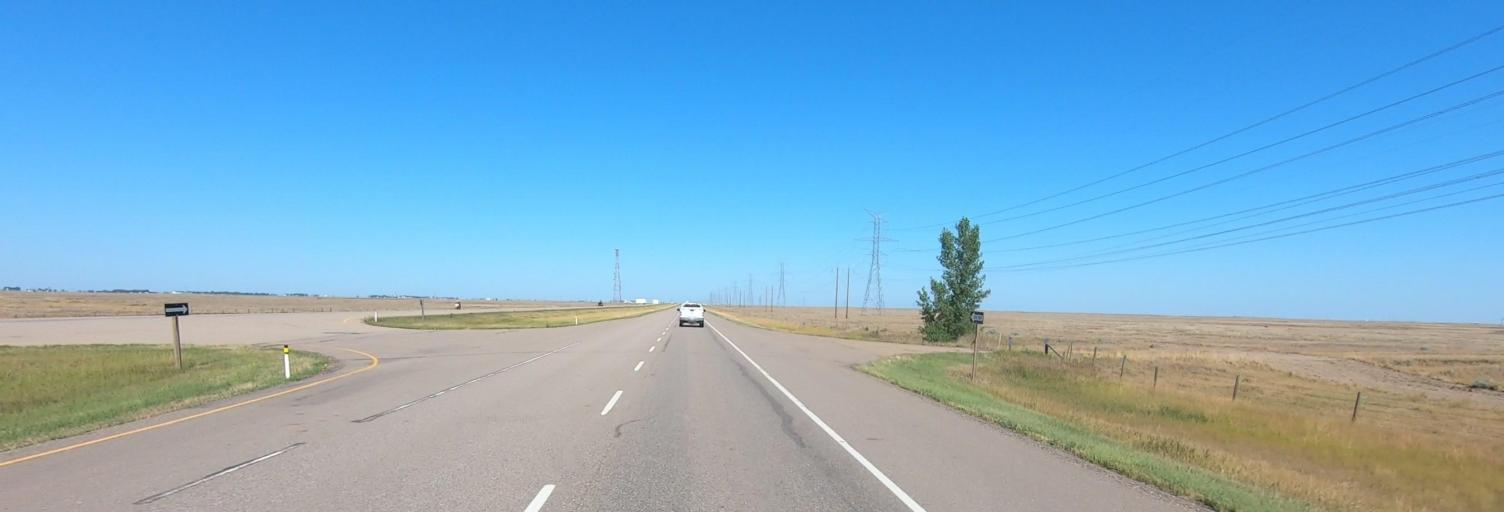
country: CA
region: Alberta
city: Brooks
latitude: 50.4369
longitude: -111.5507
